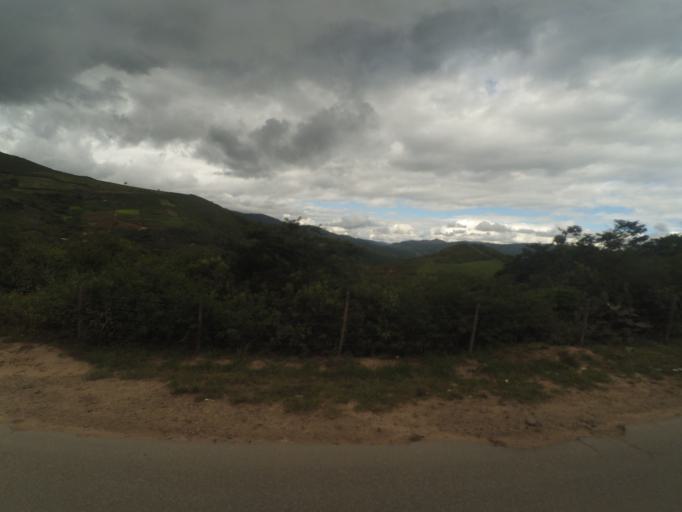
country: BO
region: Santa Cruz
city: Samaipata
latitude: -18.1756
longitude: -63.8578
